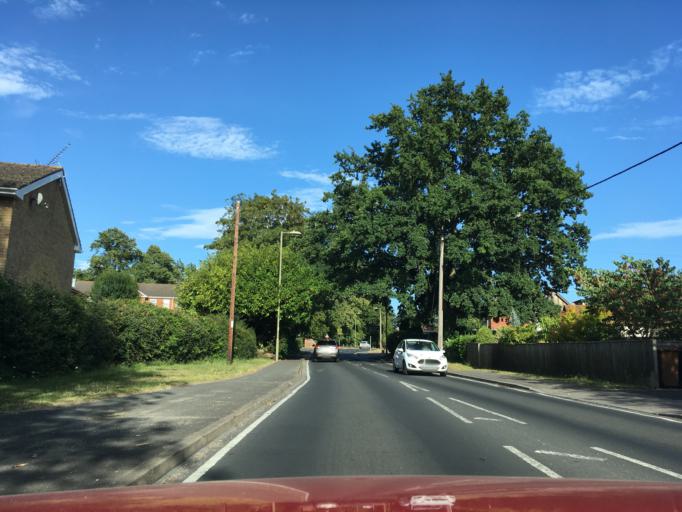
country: GB
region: England
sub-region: Hampshire
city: Romsey
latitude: 50.9877
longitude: -1.4742
